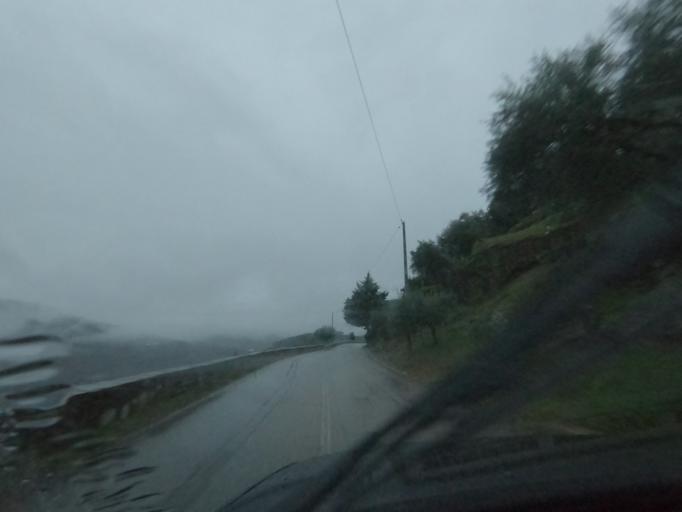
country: PT
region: Vila Real
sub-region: Sabrosa
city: Vilela
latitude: 41.2154
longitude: -7.5525
